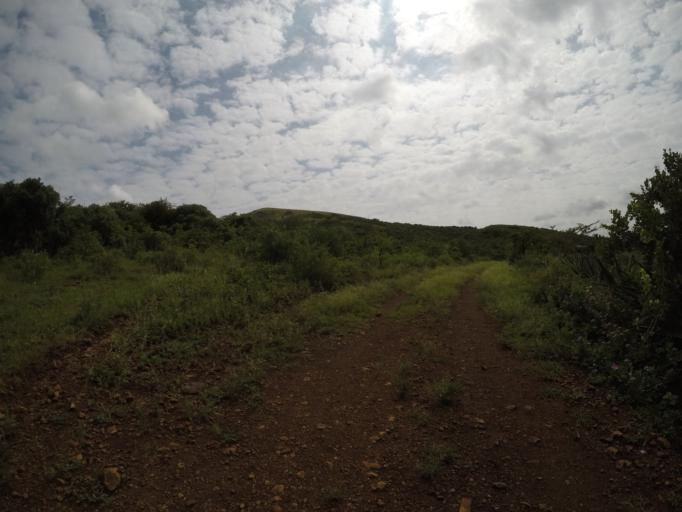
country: ZA
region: KwaZulu-Natal
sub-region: uThungulu District Municipality
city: Empangeni
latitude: -28.6123
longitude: 31.9050
